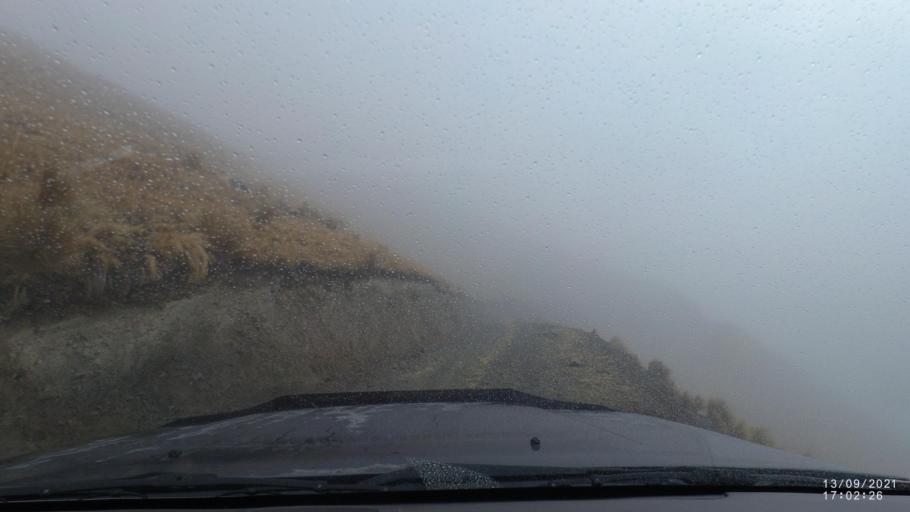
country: BO
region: Cochabamba
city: Colomi
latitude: -17.3179
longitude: -65.7222
